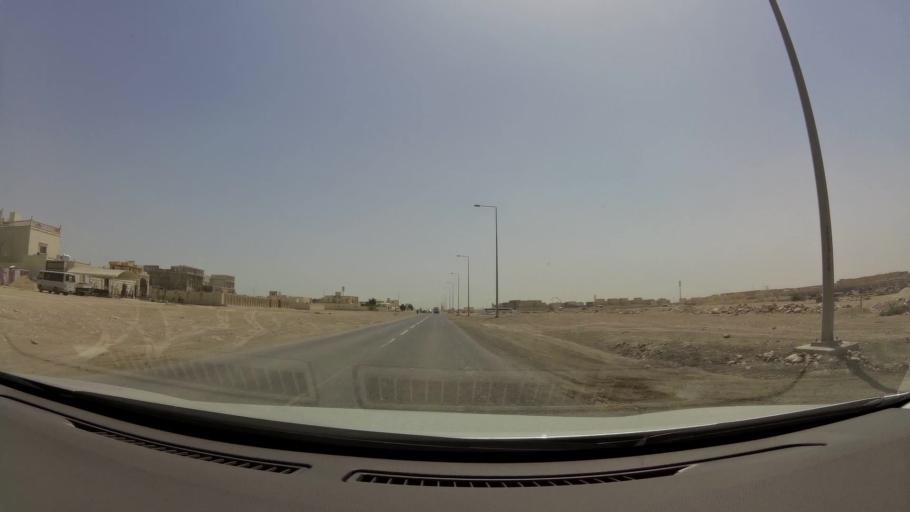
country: QA
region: Baladiyat Umm Salal
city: Umm Salal Muhammad
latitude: 25.3918
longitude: 51.4467
